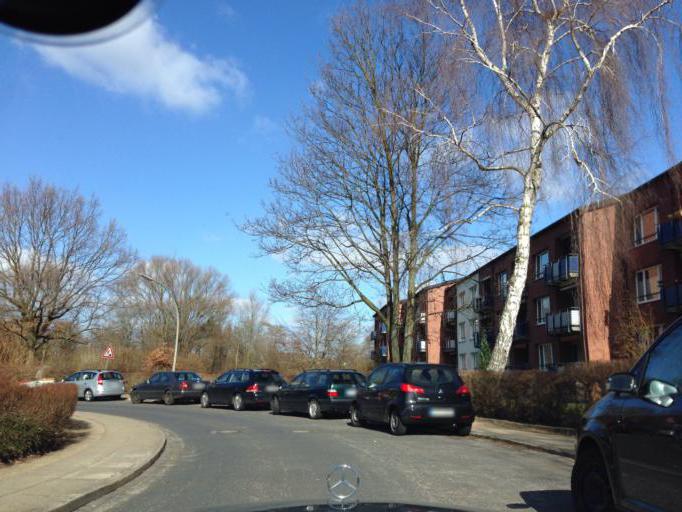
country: DE
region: Hamburg
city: Steilshoop
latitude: 53.5969
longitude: 10.0845
